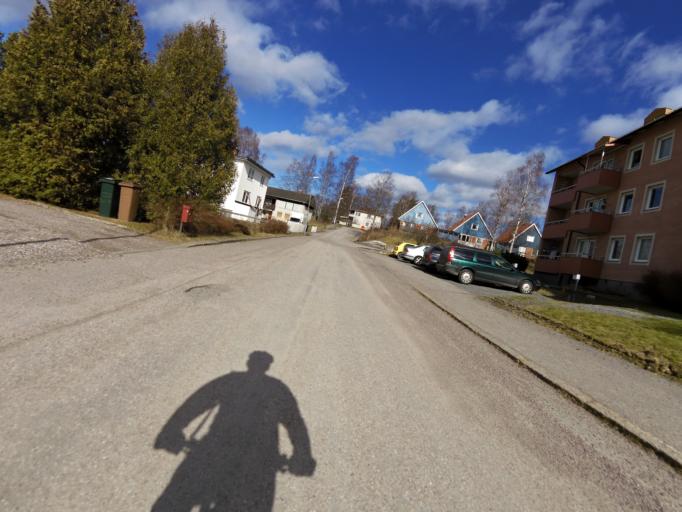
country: SE
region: Gaevleborg
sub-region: Hofors Kommun
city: Hofors
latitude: 60.5405
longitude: 16.2799
